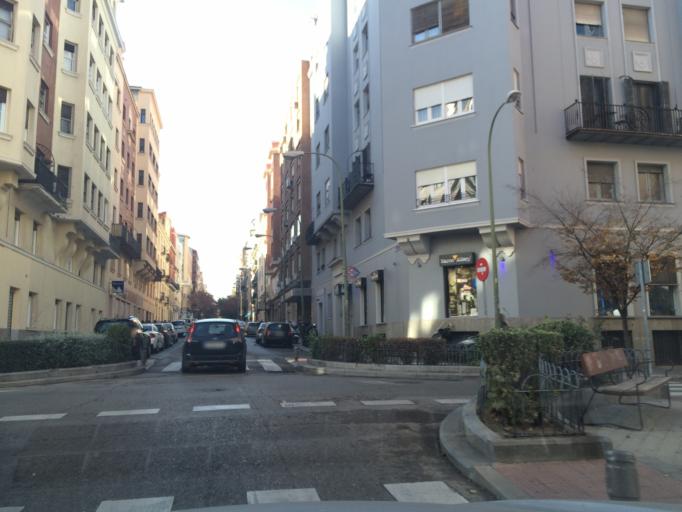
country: ES
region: Madrid
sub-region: Provincia de Madrid
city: Chamberi
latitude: 40.4395
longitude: -3.6960
